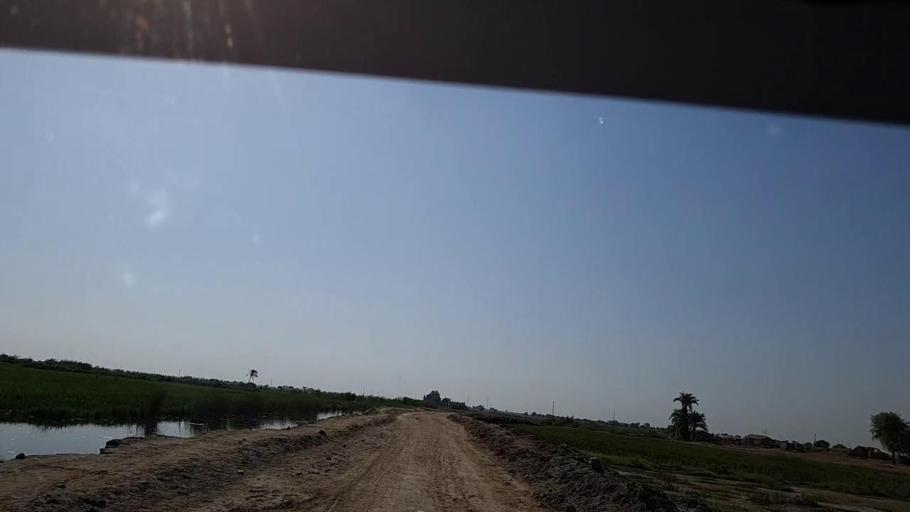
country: PK
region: Sindh
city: Tangwani
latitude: 28.3607
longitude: 69.0321
